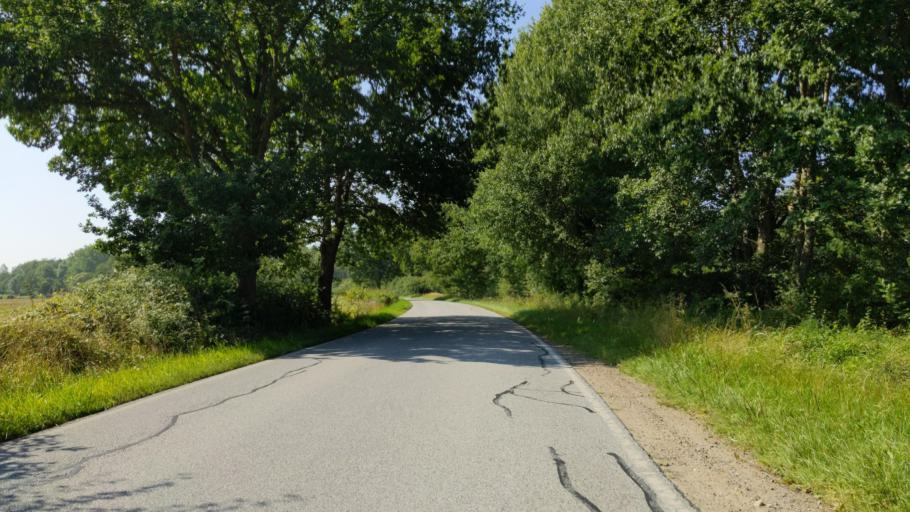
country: DE
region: Schleswig-Holstein
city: Bliestorf
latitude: 53.8042
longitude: 10.6100
